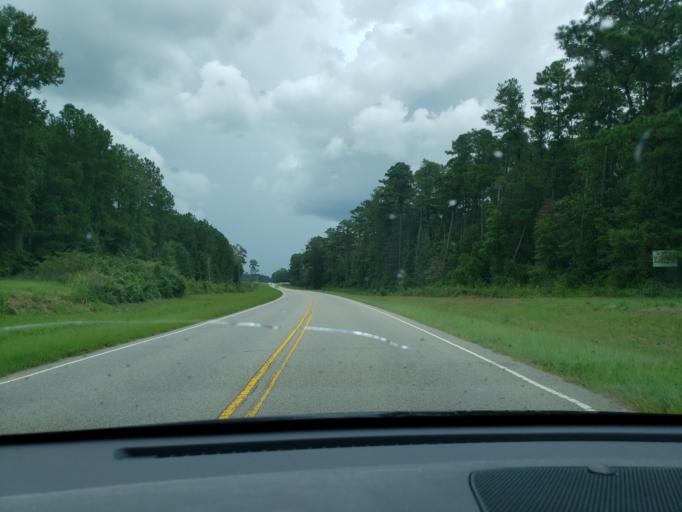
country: US
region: North Carolina
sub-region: Columbus County
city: Whiteville
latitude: 34.4705
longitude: -78.6692
